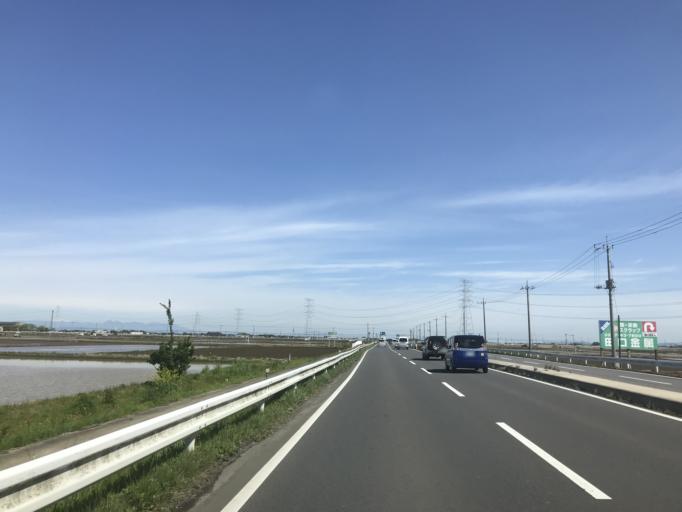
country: JP
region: Ibaraki
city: Ishige
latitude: 36.1168
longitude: 139.9831
